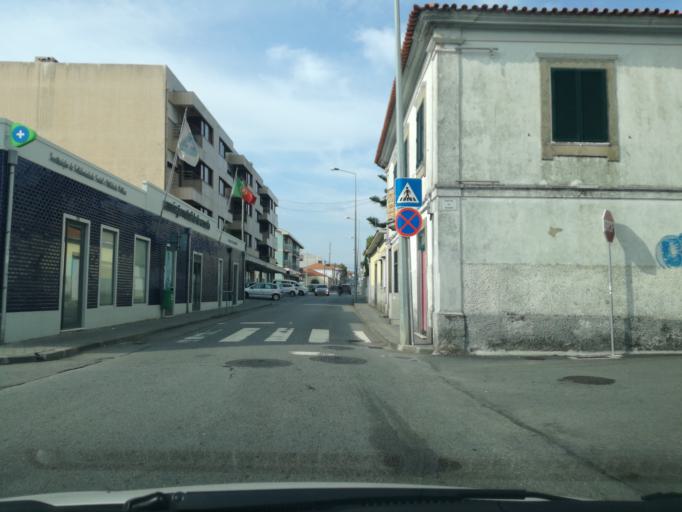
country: PT
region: Porto
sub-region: Vila Nova de Gaia
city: Sao Felix da Marinha
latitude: 41.0465
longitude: -8.6285
